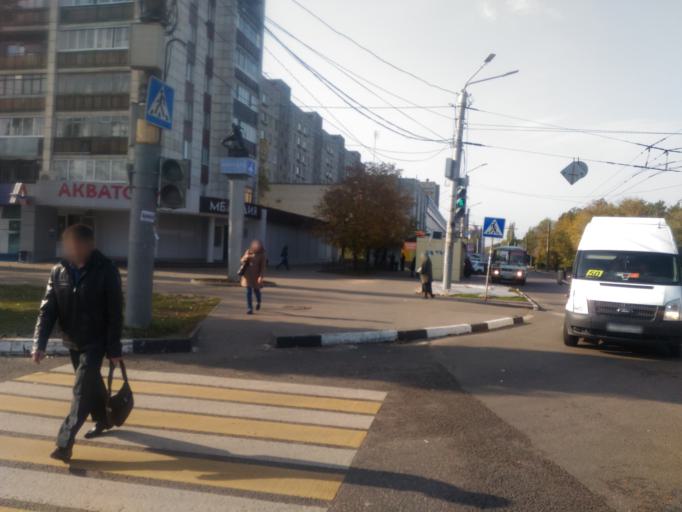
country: RU
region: Voronezj
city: Voronezh
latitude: 51.6516
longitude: 39.1355
